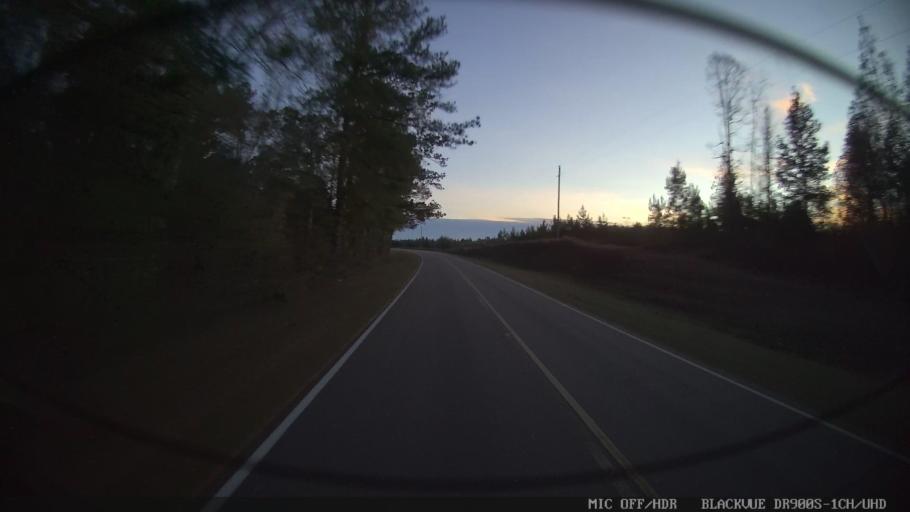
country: US
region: Mississippi
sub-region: Perry County
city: New Augusta
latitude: 31.1209
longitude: -89.1969
